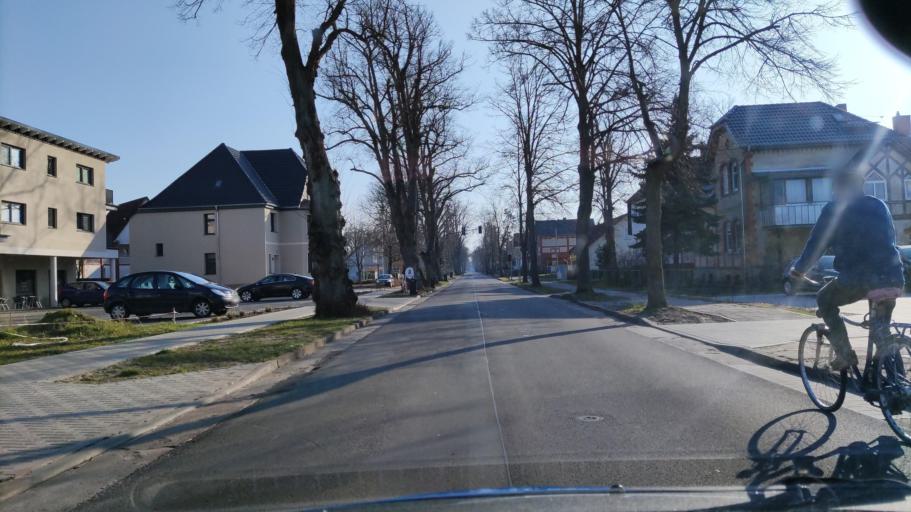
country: DE
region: Saxony-Anhalt
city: Seehausen
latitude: 52.8855
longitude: 11.7506
